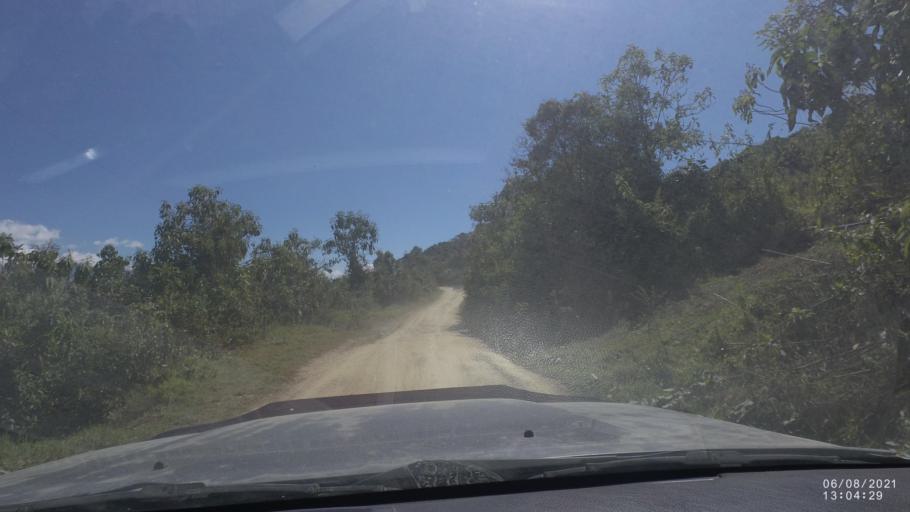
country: BO
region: La Paz
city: Quime
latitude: -16.7366
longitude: -66.6988
